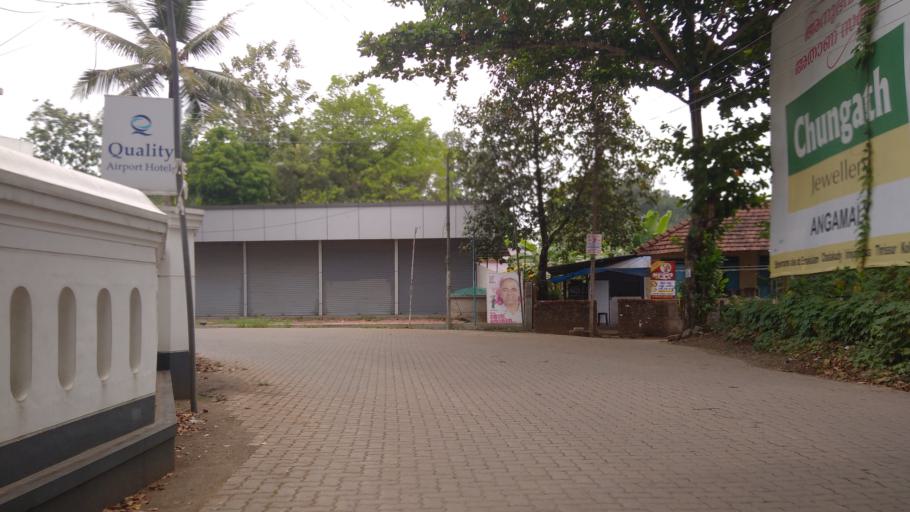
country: IN
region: Kerala
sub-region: Ernakulam
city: Angamali
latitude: 10.1659
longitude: 76.3960
